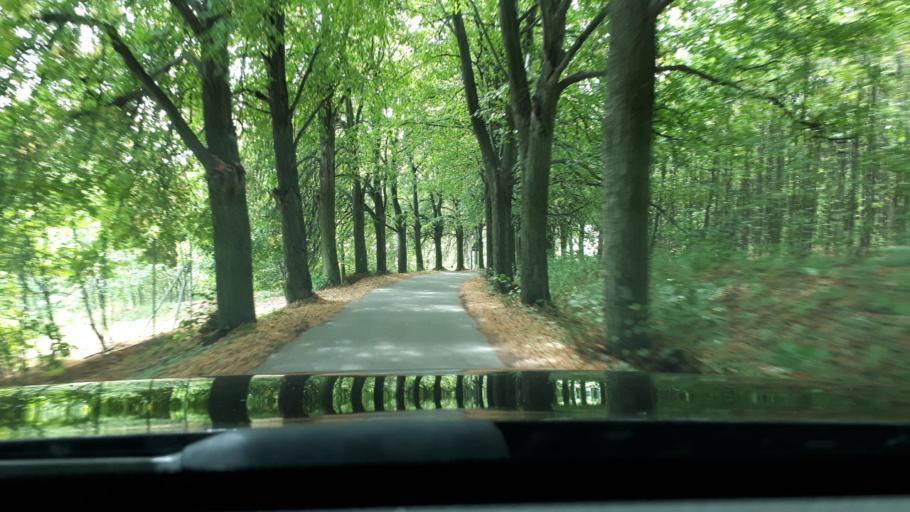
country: PL
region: Lower Silesian Voivodeship
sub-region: Powiat zlotoryjski
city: Olszanica
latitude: 51.1739
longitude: 15.7622
